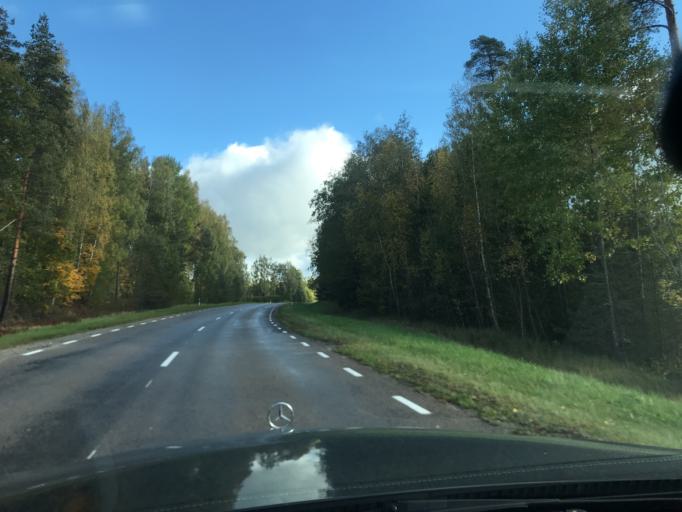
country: EE
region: Valgamaa
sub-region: Torva linn
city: Torva
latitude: 57.9891
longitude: 26.0579
